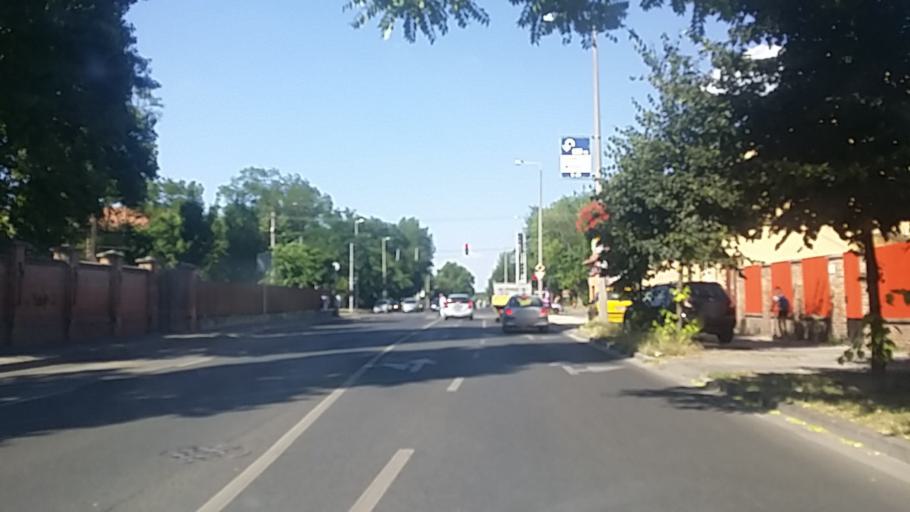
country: HU
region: Budapest
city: Budapest IV. keruelet
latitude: 47.5794
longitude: 19.0876
